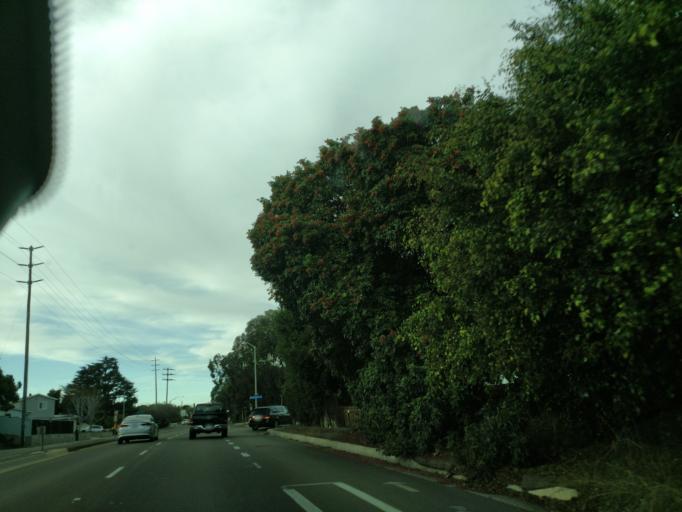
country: US
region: California
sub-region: San Diego County
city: Coronado
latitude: 32.7352
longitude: -117.2296
